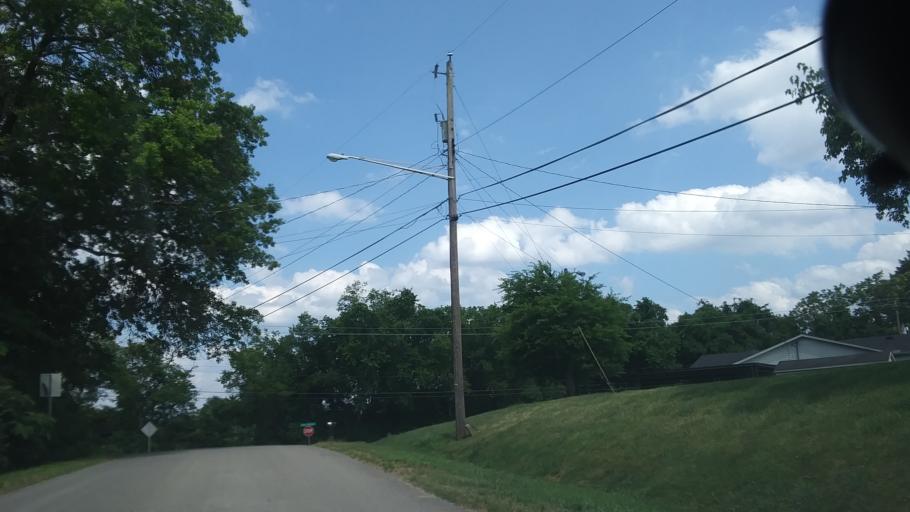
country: US
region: Tennessee
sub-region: Rutherford County
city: La Vergne
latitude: 36.0902
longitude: -86.6620
